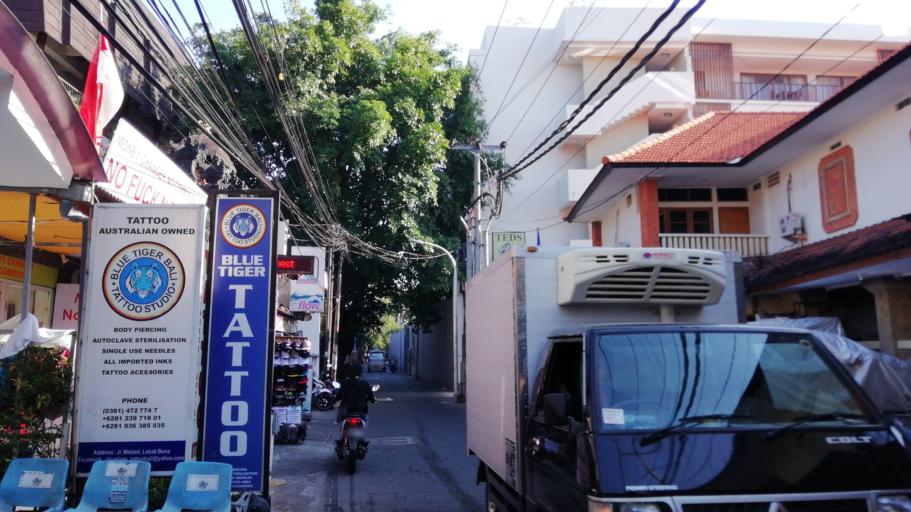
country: ID
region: Bali
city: Kuta
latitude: -8.7100
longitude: 115.1702
